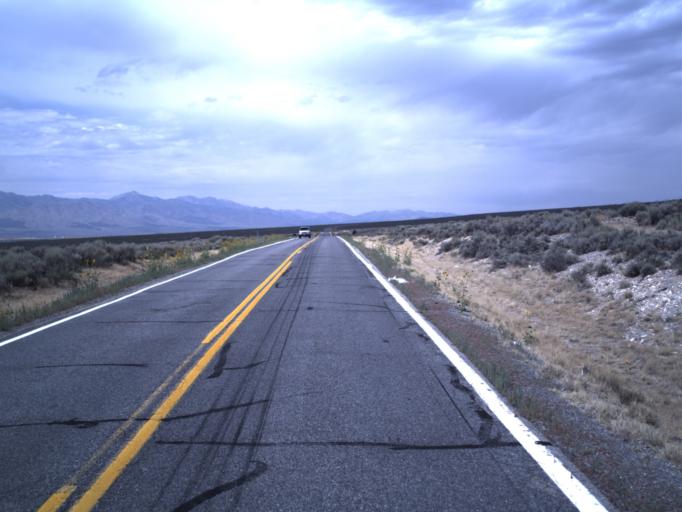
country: US
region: Utah
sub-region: Utah County
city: Eagle Mountain
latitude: 40.2753
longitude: -112.2506
